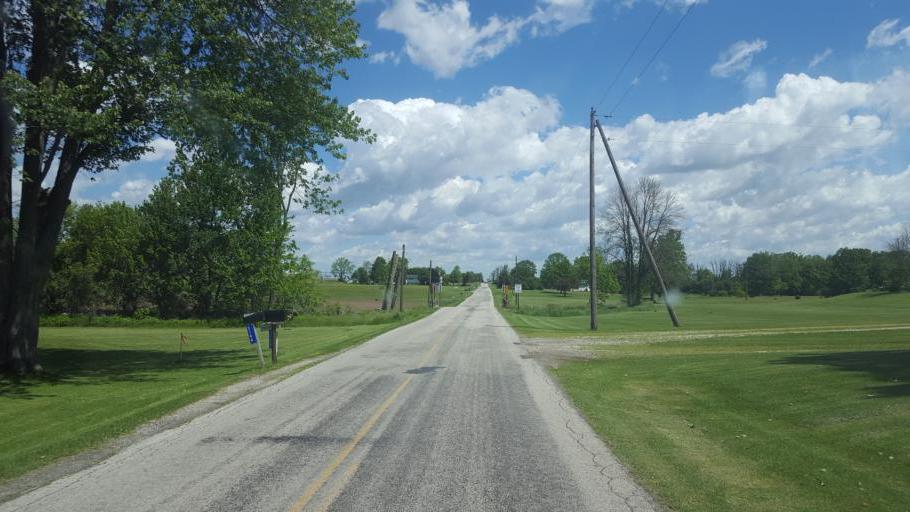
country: US
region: Ohio
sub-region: Richland County
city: Shelby
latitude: 40.8398
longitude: -82.6774
